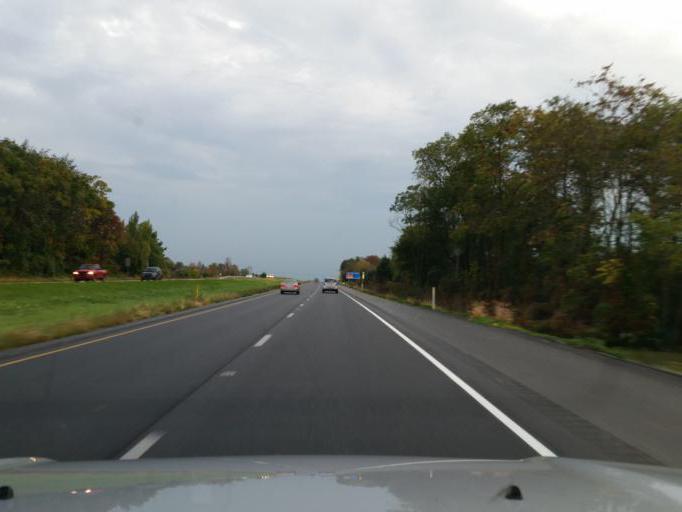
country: US
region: Pennsylvania
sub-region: Adams County
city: Gettysburg
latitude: 39.8564
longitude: -77.1979
